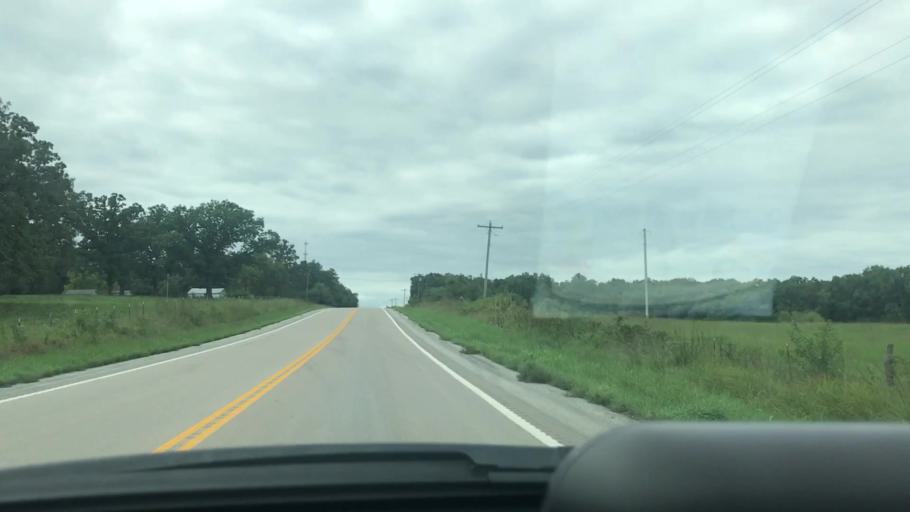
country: US
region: Missouri
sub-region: Benton County
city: Warsaw
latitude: 38.1397
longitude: -93.2860
